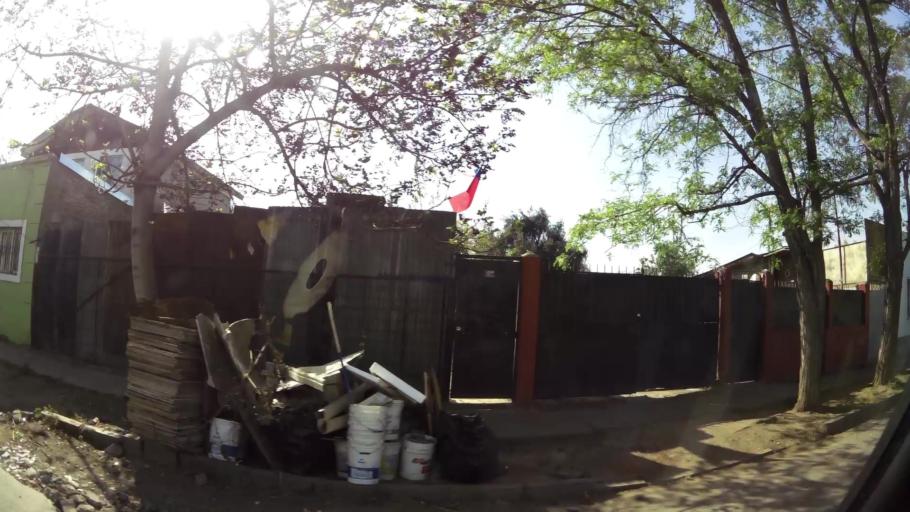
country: CL
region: Santiago Metropolitan
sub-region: Provincia de Santiago
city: Lo Prado
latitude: -33.4250
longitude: -70.7244
